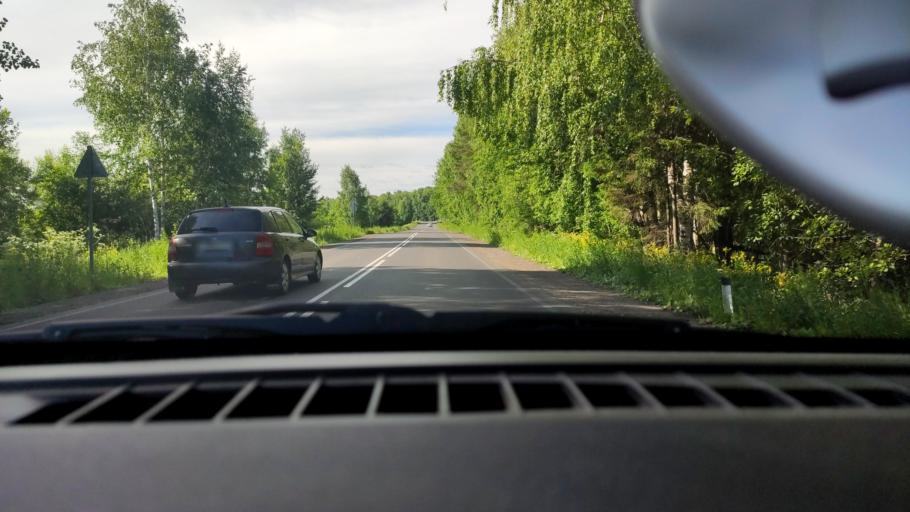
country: RU
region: Perm
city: Nytva
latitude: 57.9279
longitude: 55.4497
